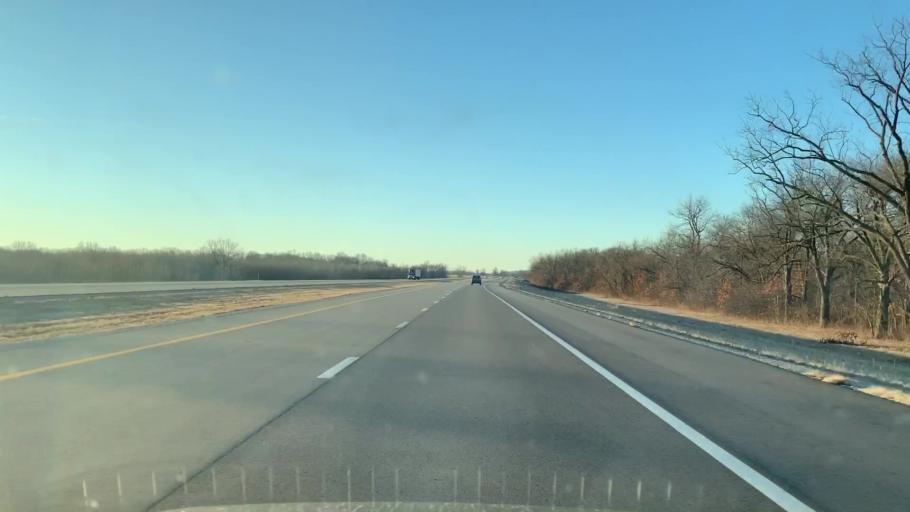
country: US
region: Kansas
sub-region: Linn County
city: La Cygne
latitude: 38.3076
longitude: -94.6777
